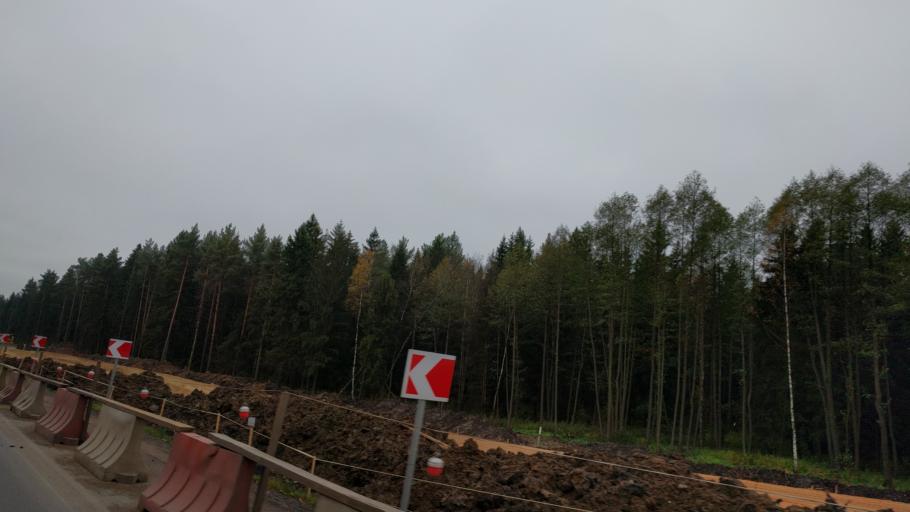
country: RU
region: Moskovskaya
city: Golitsyno
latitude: 55.5847
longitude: 37.0018
